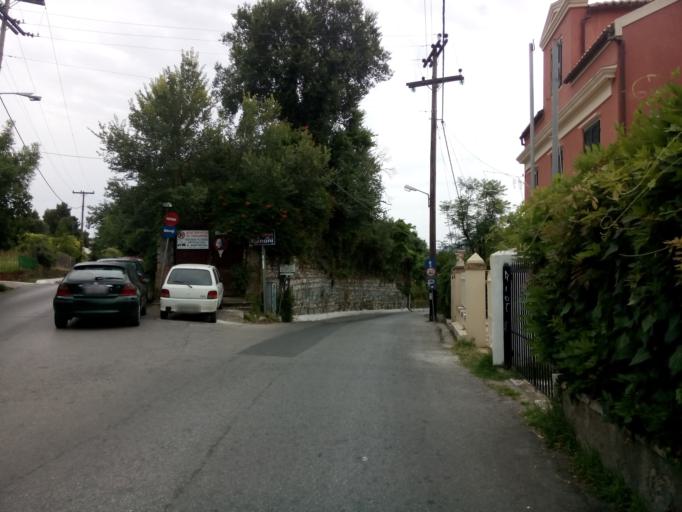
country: GR
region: Ionian Islands
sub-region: Nomos Kerkyras
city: Kerkyra
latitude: 39.6060
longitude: 19.9212
